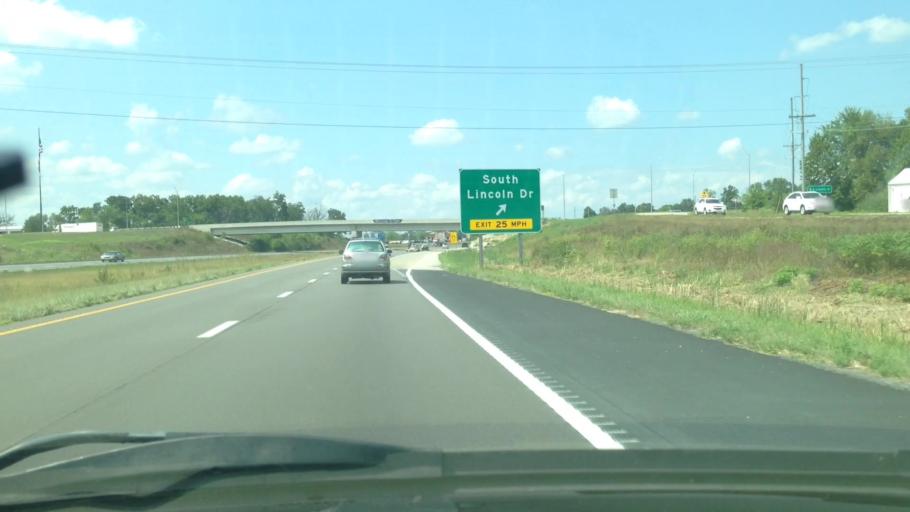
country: US
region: Missouri
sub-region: Lincoln County
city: Troy
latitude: 38.9654
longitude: -90.9547
